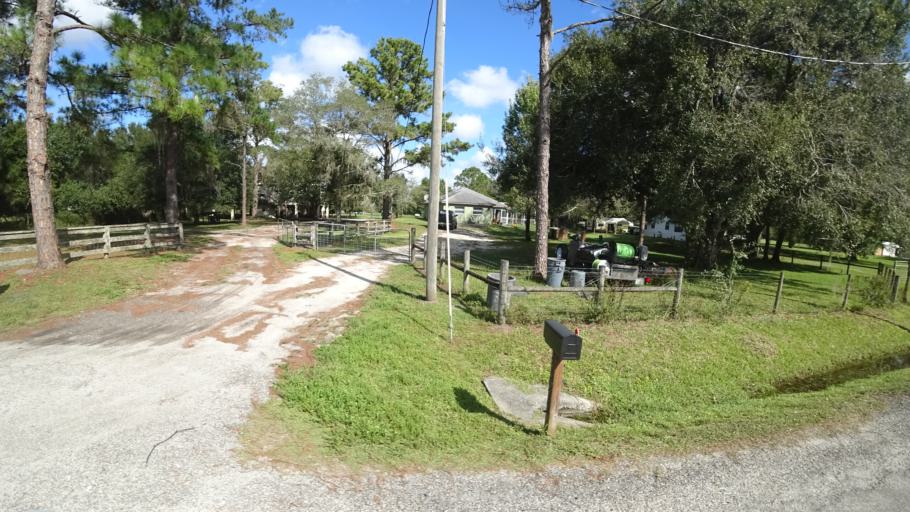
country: US
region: Florida
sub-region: Sarasota County
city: Lake Sarasota
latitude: 27.3555
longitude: -82.1566
